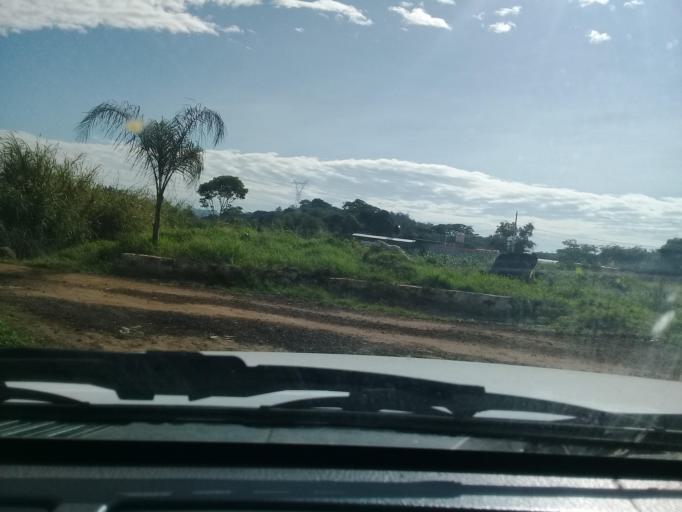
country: MX
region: Veracruz
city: El Castillo
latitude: 19.5445
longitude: -96.8789
